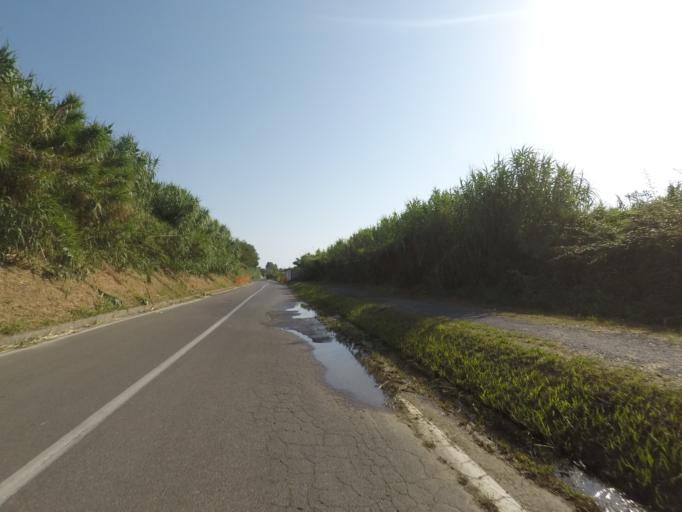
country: IT
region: Liguria
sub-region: Provincia di La Spezia
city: Casano-Dogana-Isola
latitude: 44.0574
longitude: 10.0271
